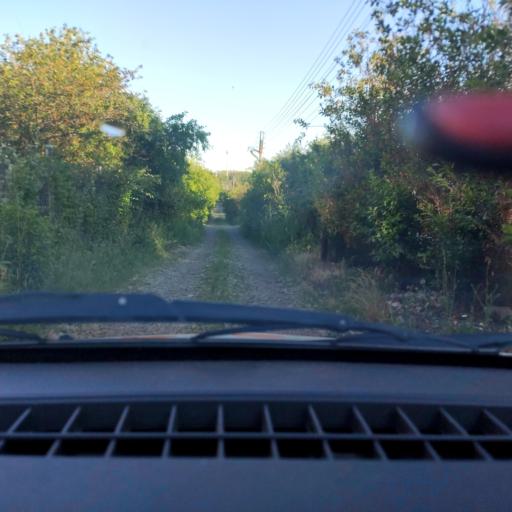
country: RU
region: Bashkortostan
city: Karmaskaly
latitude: 54.3678
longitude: 55.9031
